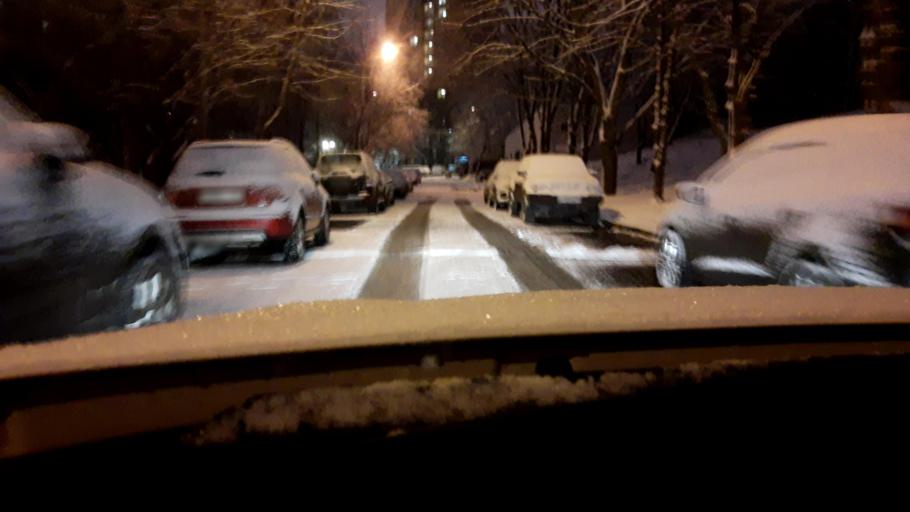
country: RU
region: Moscow
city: Vorob'yovo
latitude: 55.7173
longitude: 37.5219
